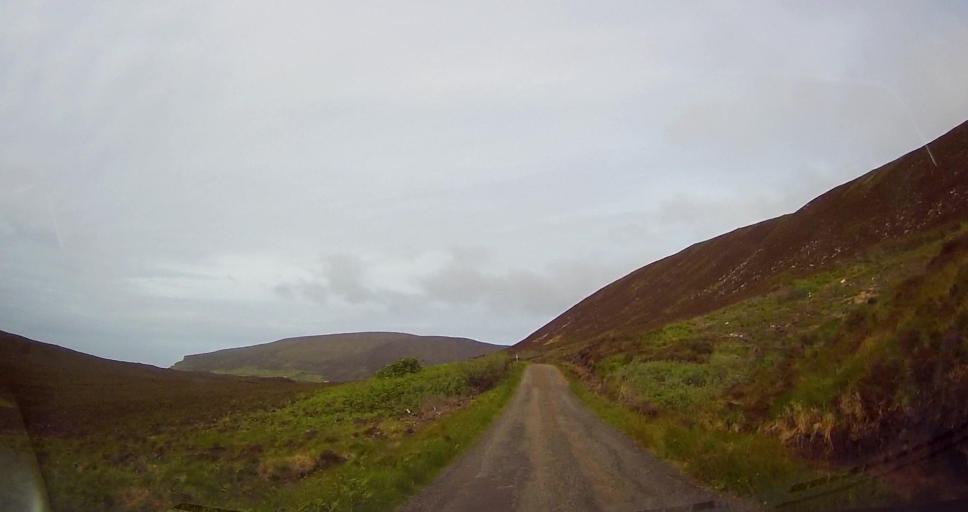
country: GB
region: Scotland
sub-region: Orkney Islands
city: Stromness
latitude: 58.8818
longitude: -3.3523
